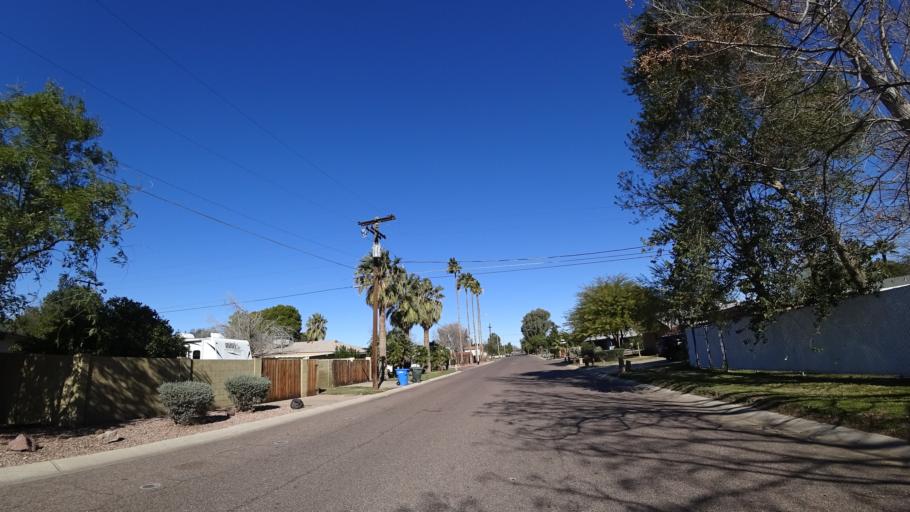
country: US
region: Arizona
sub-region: Maricopa County
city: Phoenix
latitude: 33.5188
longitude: -112.0606
